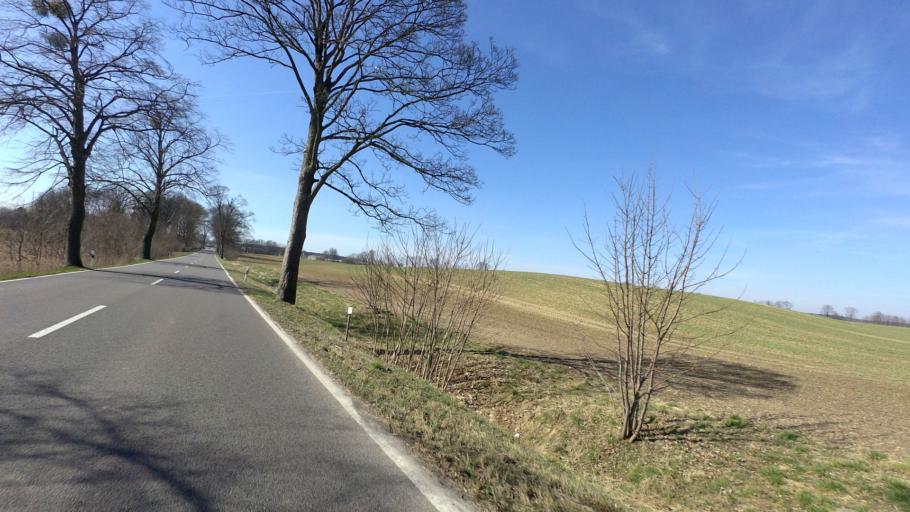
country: DE
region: Brandenburg
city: Protzel
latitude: 52.6362
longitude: 13.9990
